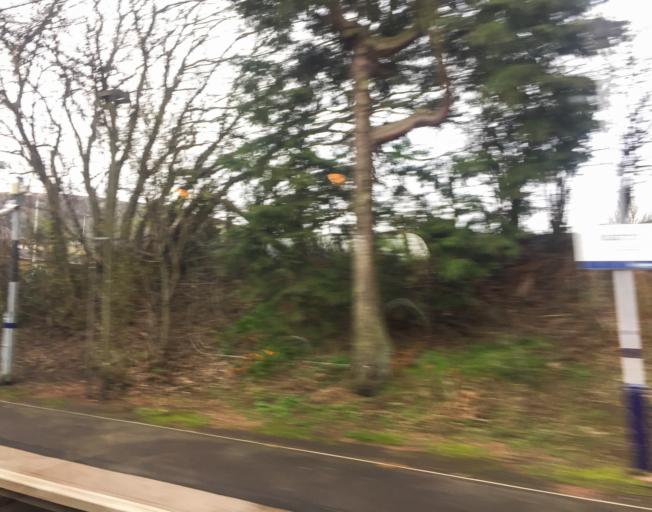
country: GB
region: Scotland
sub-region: West Dunbartonshire
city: Old Kilpatrick
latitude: 55.9236
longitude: -4.4519
